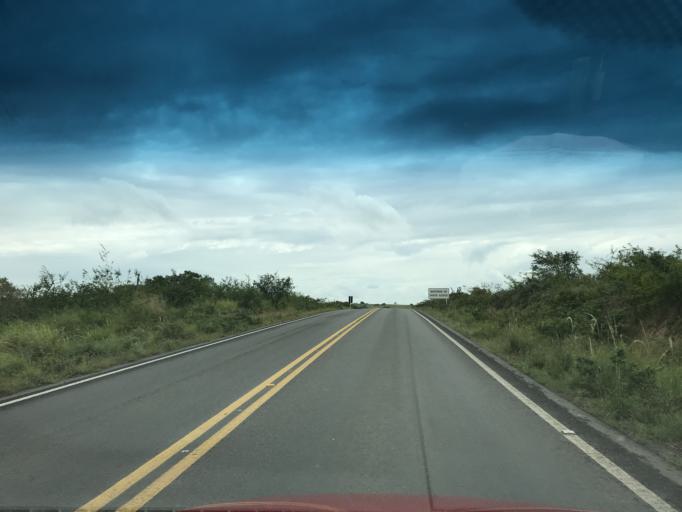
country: BR
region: Bahia
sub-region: Castro Alves
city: Castro Alves
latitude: -12.7565
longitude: -39.4140
